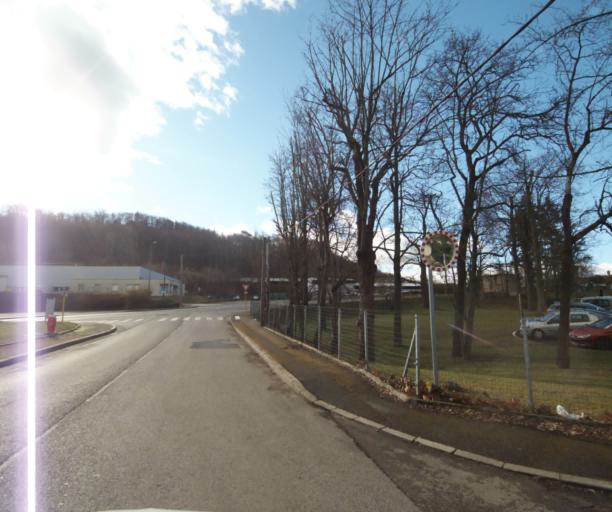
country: FR
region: Rhone-Alpes
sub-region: Departement de la Loire
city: La Talaudiere
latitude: 45.4689
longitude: 4.4334
